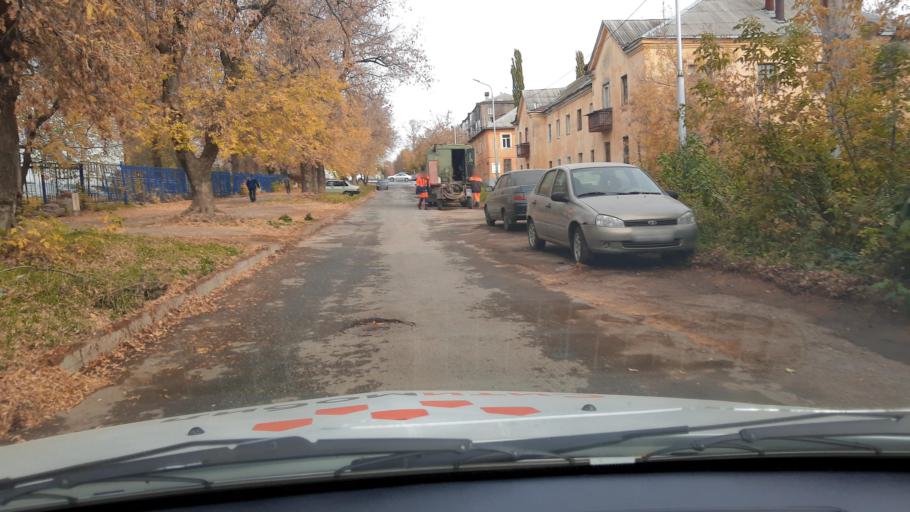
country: RU
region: Bashkortostan
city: Ufa
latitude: 54.8122
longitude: 56.0761
